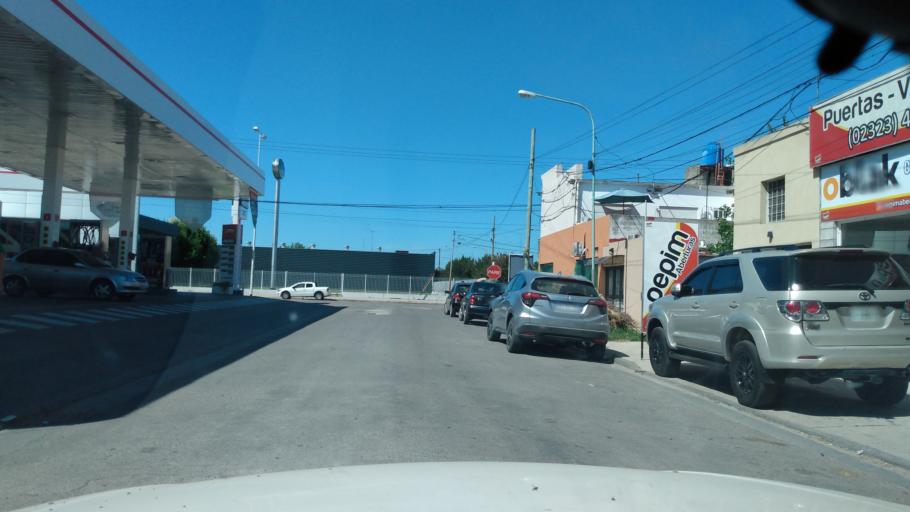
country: AR
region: Buenos Aires
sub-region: Partido de Lujan
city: Lujan
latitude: -34.5613
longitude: -59.1061
